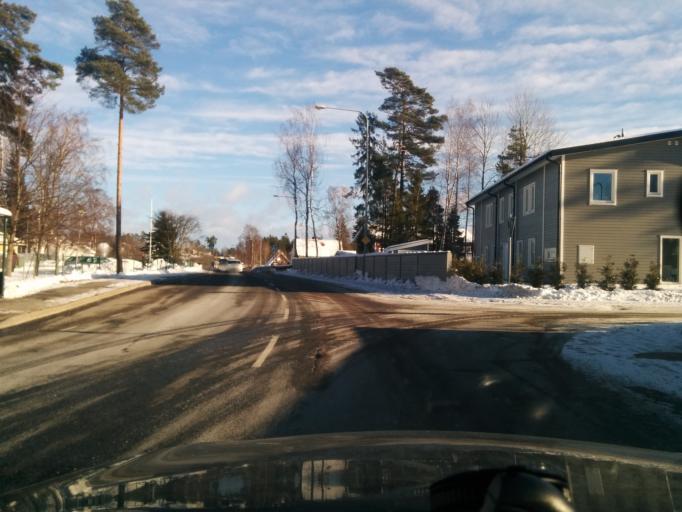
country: SE
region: Stockholm
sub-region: Vallentuna Kommun
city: Vallentuna
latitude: 59.4967
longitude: 18.0783
